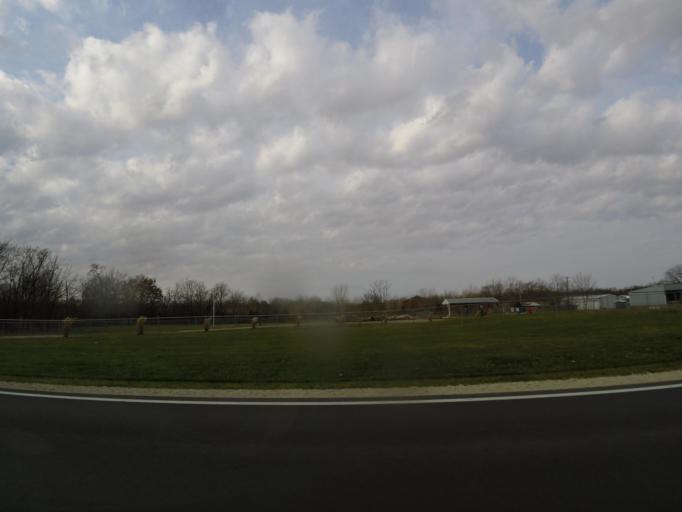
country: US
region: Illinois
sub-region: Christian County
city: Pana
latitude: 39.3728
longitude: -89.0817
